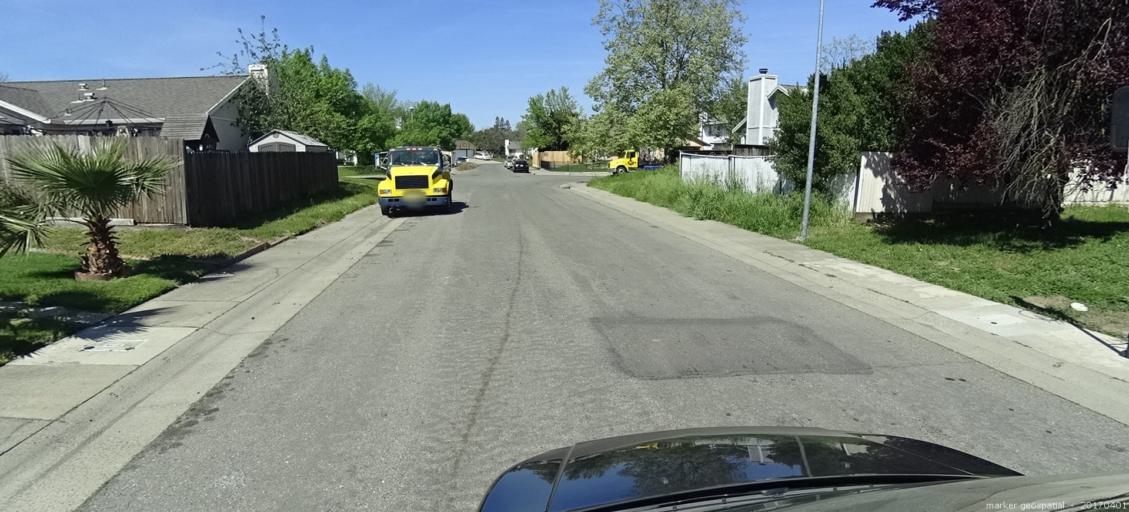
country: US
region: California
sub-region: Sacramento County
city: Laguna
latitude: 38.4473
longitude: -121.4331
